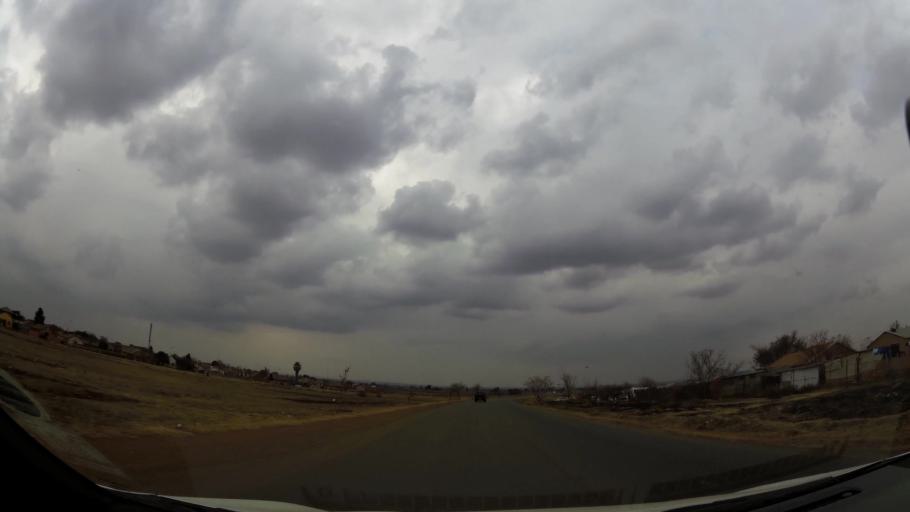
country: ZA
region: Gauteng
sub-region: Ekurhuleni Metropolitan Municipality
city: Germiston
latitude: -26.3829
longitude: 28.1367
